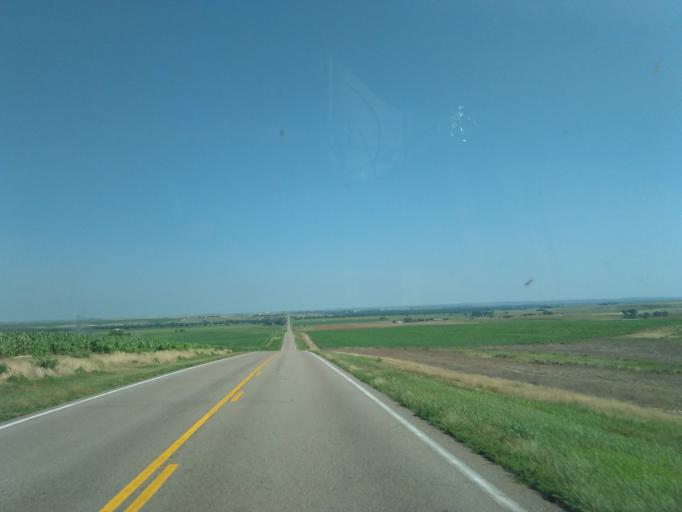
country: US
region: Nebraska
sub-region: Dundy County
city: Benkelman
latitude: 39.9785
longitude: -101.5419
